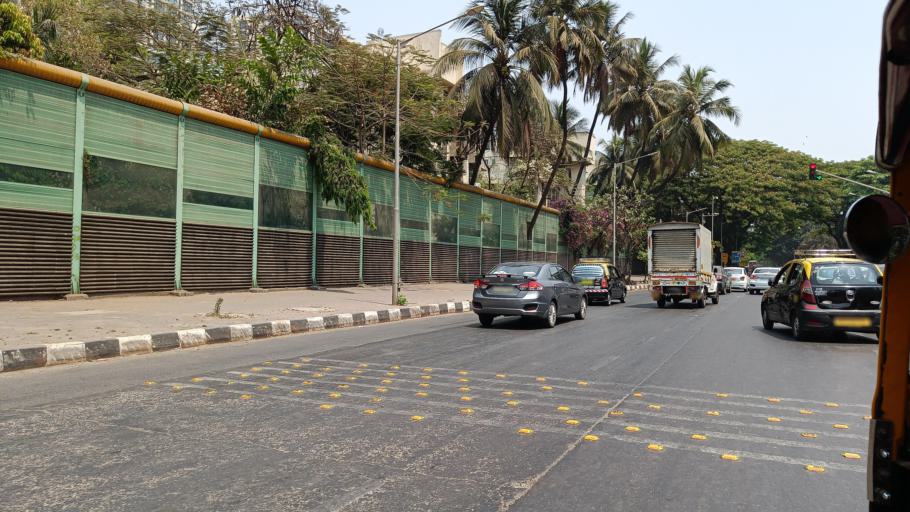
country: IN
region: Maharashtra
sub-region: Mumbai Suburban
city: Mumbai
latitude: 19.0554
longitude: 72.8503
